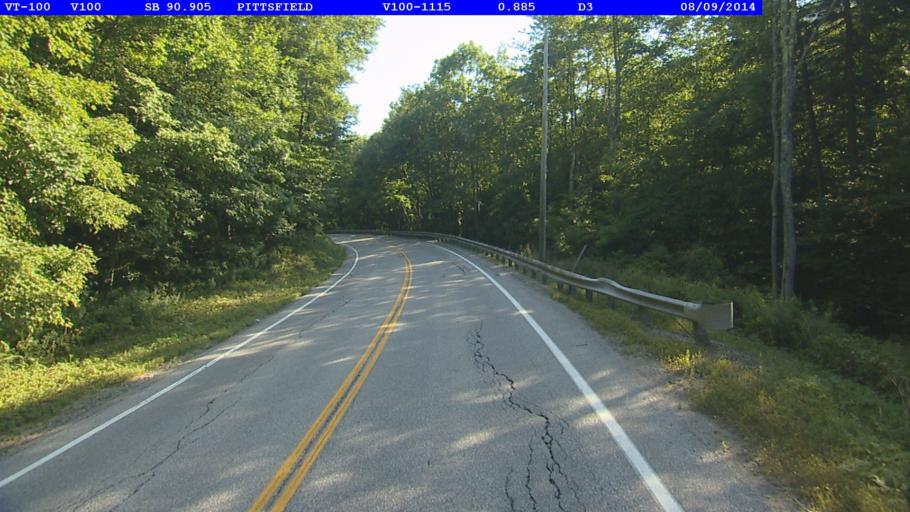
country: US
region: Vermont
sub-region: Rutland County
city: Rutland
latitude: 43.7301
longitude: -72.8225
